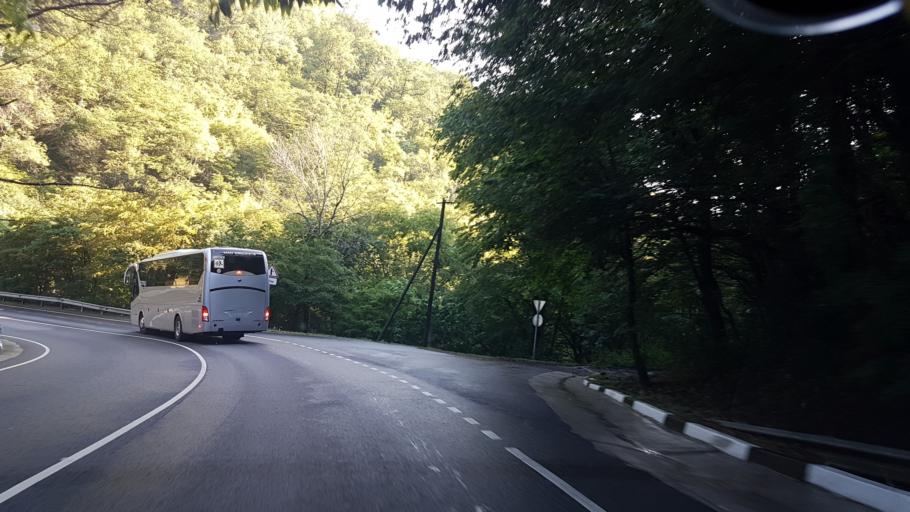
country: RU
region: Krasnodarskiy
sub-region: Sochi City
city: Lazarevskoye
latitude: 43.8434
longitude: 39.4172
